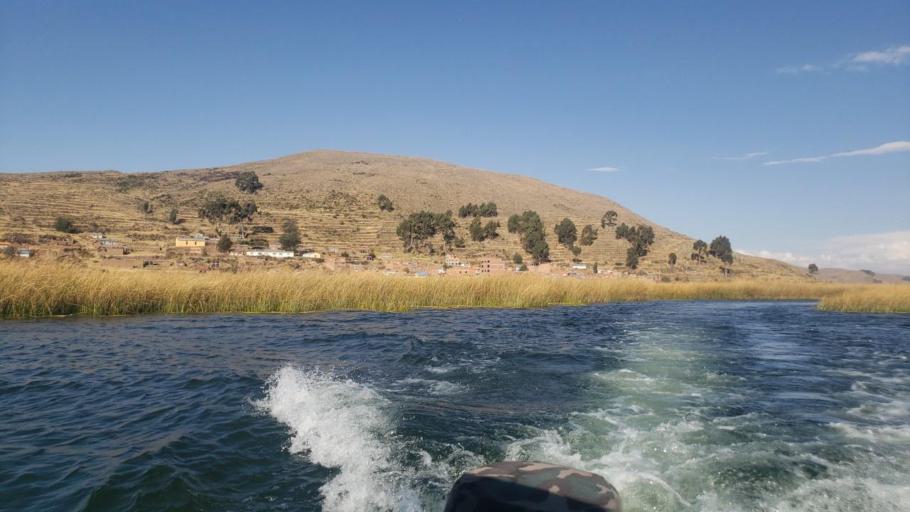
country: BO
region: La Paz
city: Huatajata
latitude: -16.3285
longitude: -68.7203
